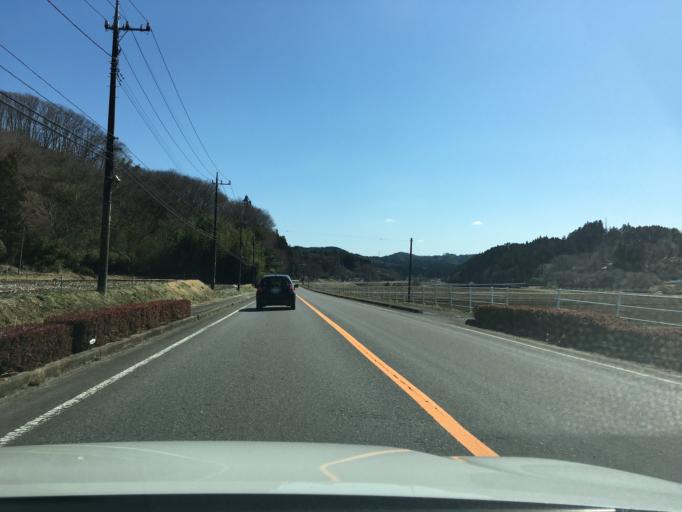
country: JP
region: Tochigi
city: Kuroiso
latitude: 37.0302
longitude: 140.1741
